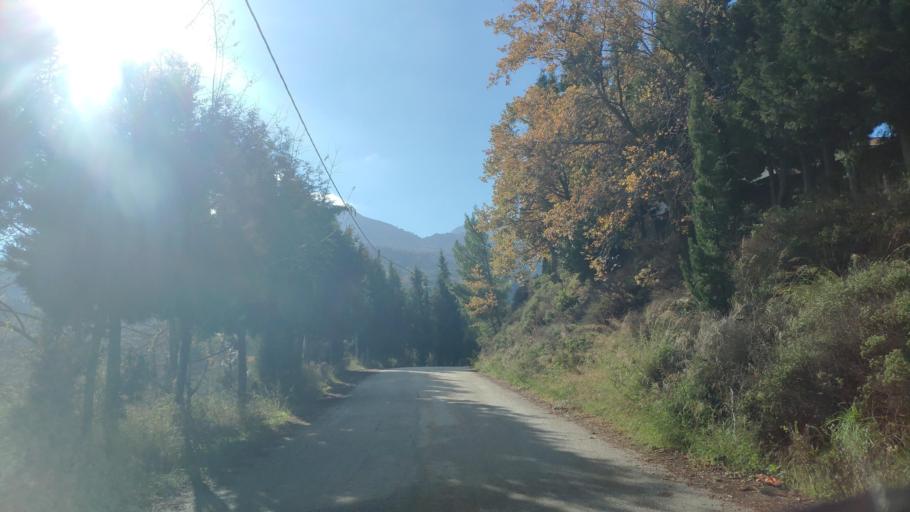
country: GR
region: West Greece
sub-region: Nomos Achaias
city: Aiyira
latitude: 38.0942
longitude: 22.4401
